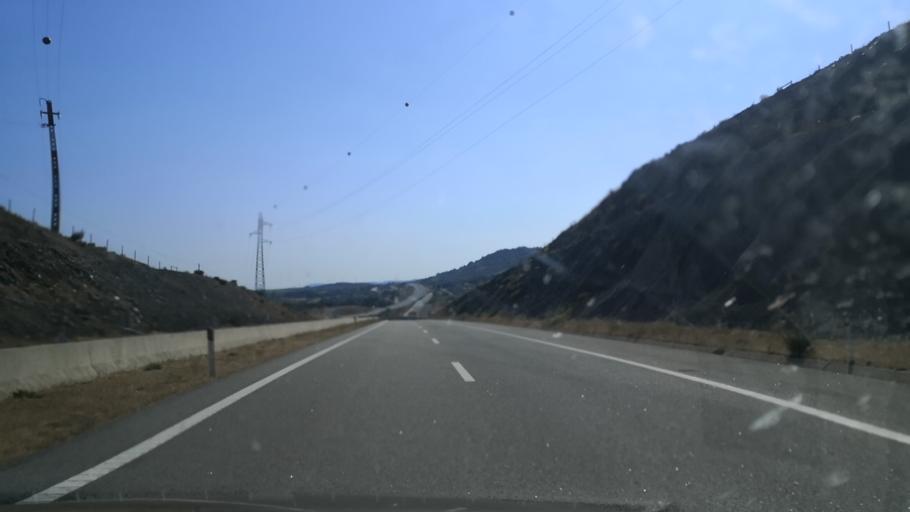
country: PT
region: Braganca
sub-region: Macedo de Cavaleiros
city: Macedo de Cavaleiros
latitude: 41.6285
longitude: -6.8510
